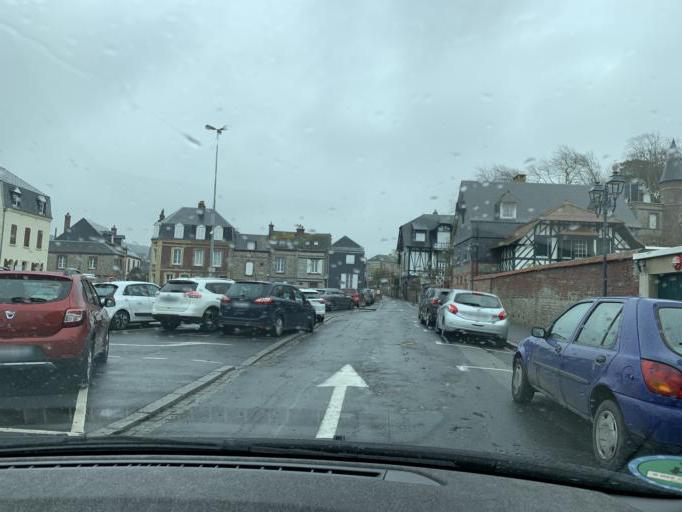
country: FR
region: Haute-Normandie
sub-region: Departement de la Seine-Maritime
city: Etretat
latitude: 49.7072
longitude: 0.2015
